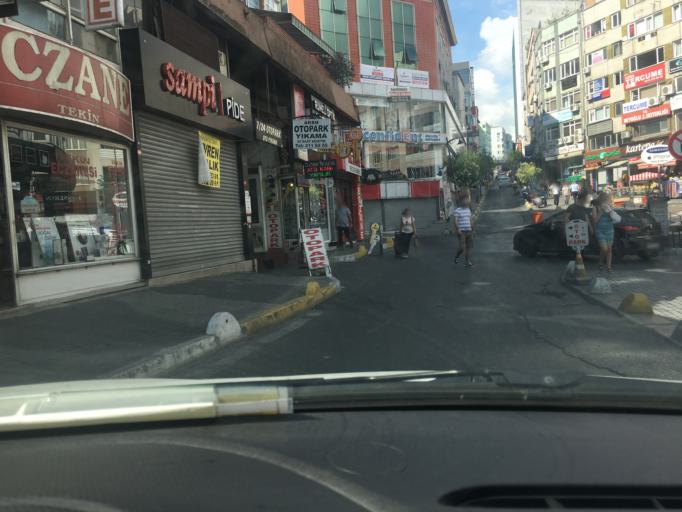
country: TR
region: Istanbul
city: Sisli
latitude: 41.0680
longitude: 28.9990
